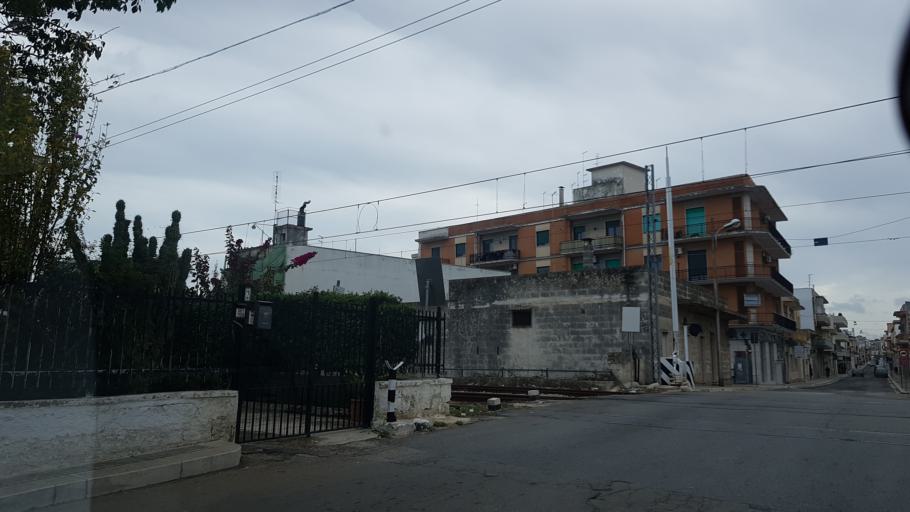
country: IT
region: Apulia
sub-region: Provincia di Brindisi
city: Mesagne
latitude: 40.5643
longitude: 17.8039
